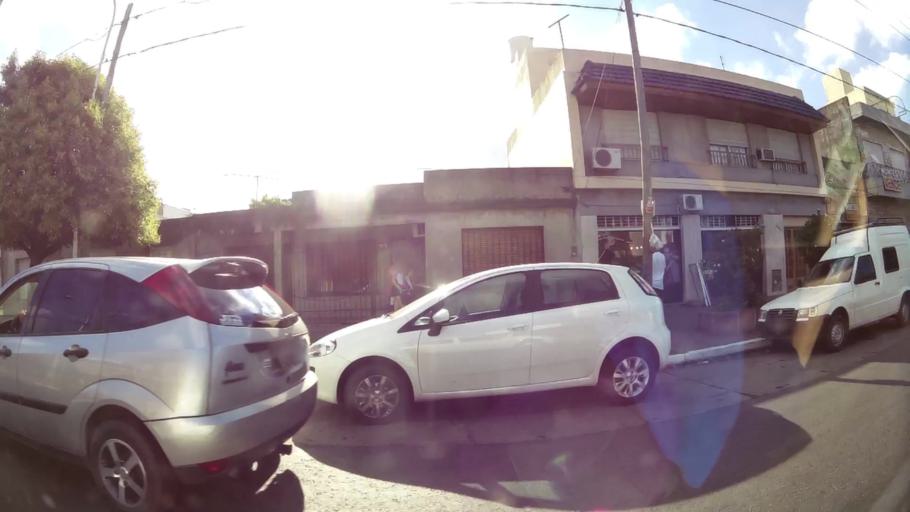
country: AR
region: Buenos Aires
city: San Justo
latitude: -34.6984
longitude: -58.5864
